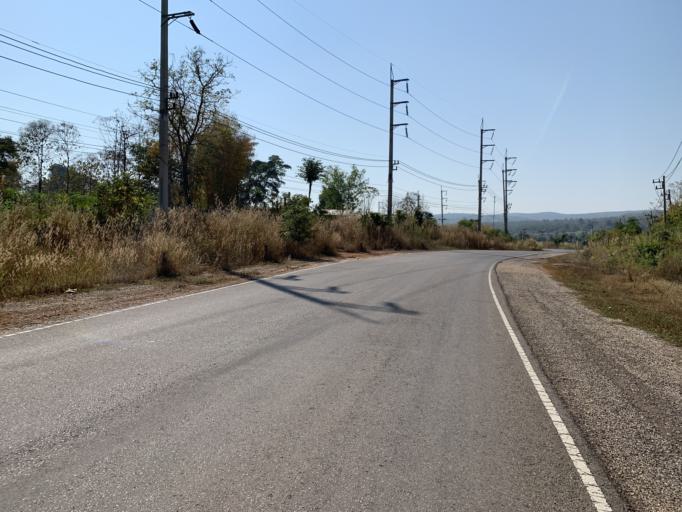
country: TH
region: Phitsanulok
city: Chat Trakan
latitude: 17.2022
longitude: 100.3936
